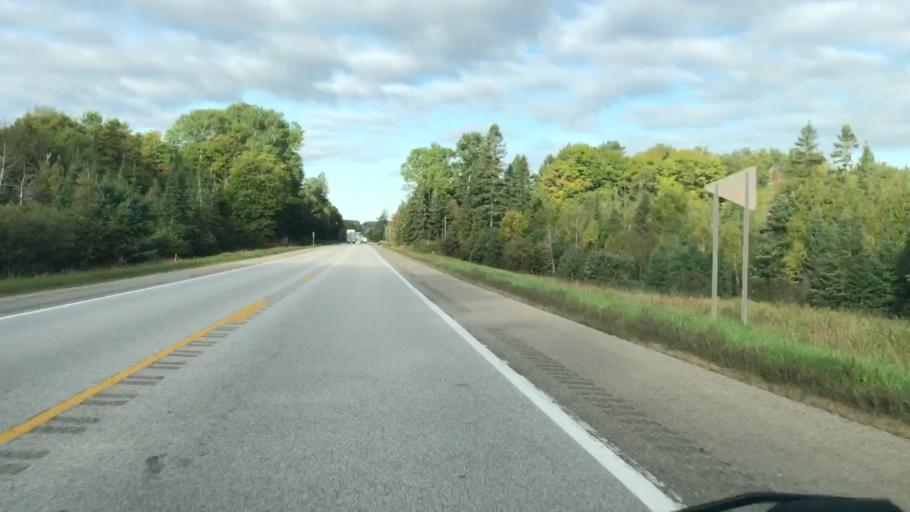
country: US
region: Michigan
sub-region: Luce County
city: Newberry
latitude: 46.3319
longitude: -85.0604
